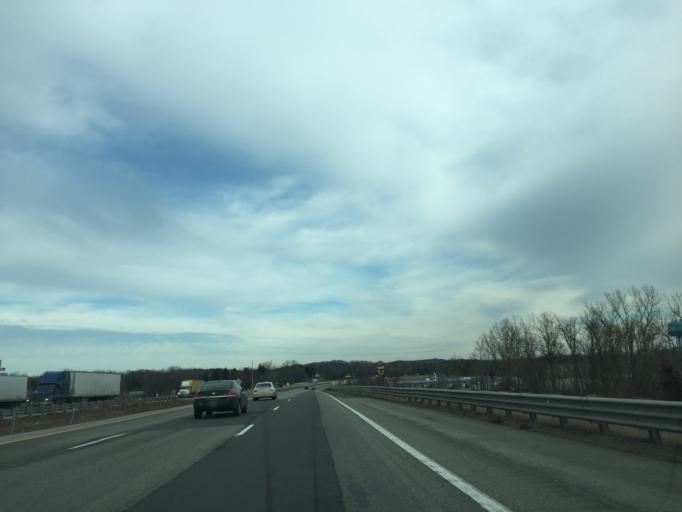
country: US
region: Michigan
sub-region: Berrien County
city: Shorewood-Tower Hills-Harbert
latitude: 41.8807
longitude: -86.6014
